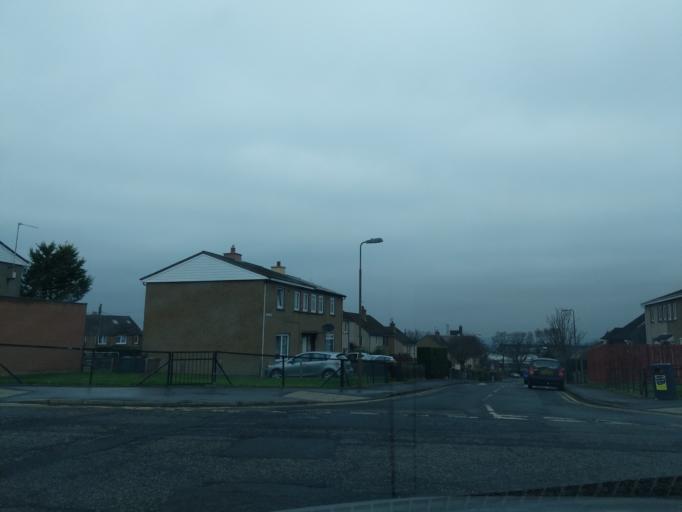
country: GB
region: Scotland
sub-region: Edinburgh
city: Currie
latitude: 55.8943
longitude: -3.3183
